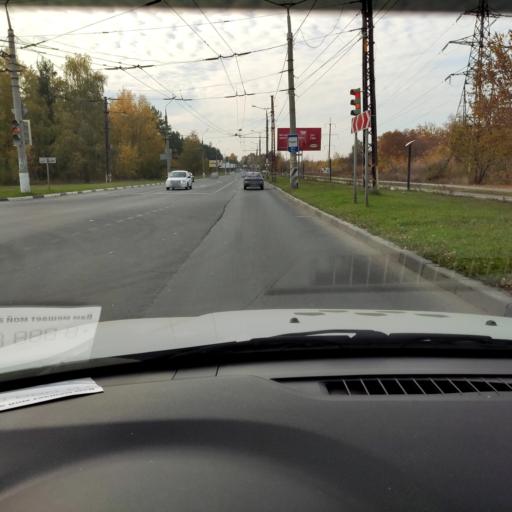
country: RU
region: Samara
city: Tol'yatti
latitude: 53.4991
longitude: 49.3888
